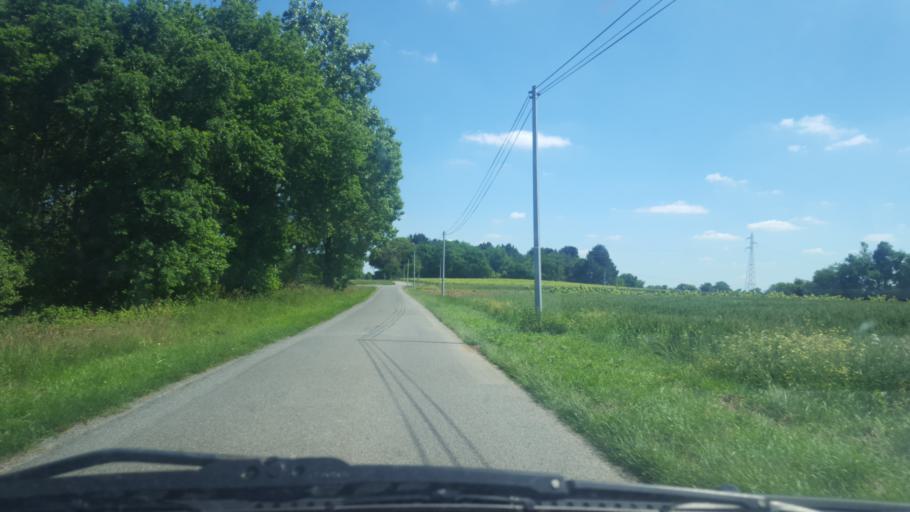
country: FR
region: Pays de la Loire
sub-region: Departement de la Loire-Atlantique
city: La Limouziniere
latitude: 47.0157
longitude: -1.6133
